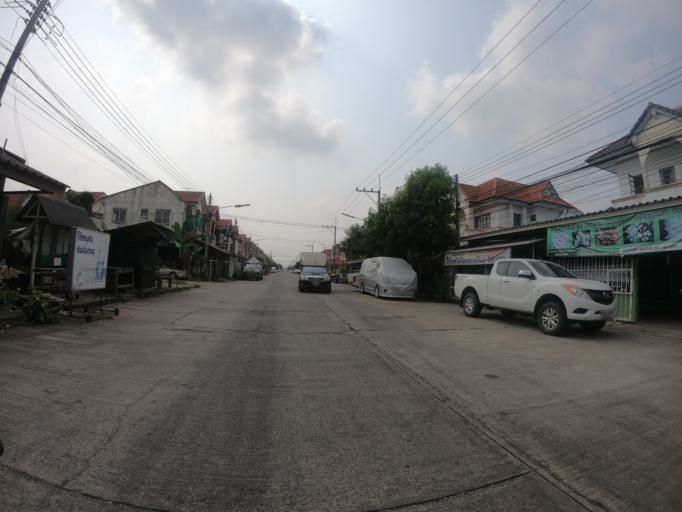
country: TH
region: Pathum Thani
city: Nong Suea
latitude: 14.0733
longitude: 100.8585
